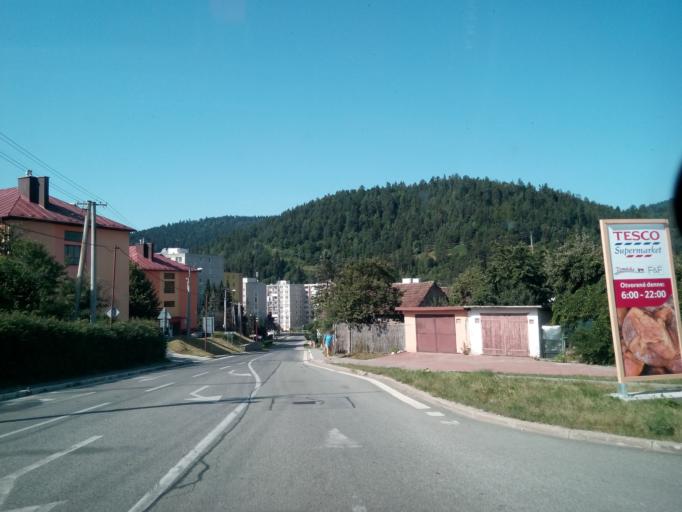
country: SK
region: Kosicky
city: Krompachy
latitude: 48.9176
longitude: 20.8761
